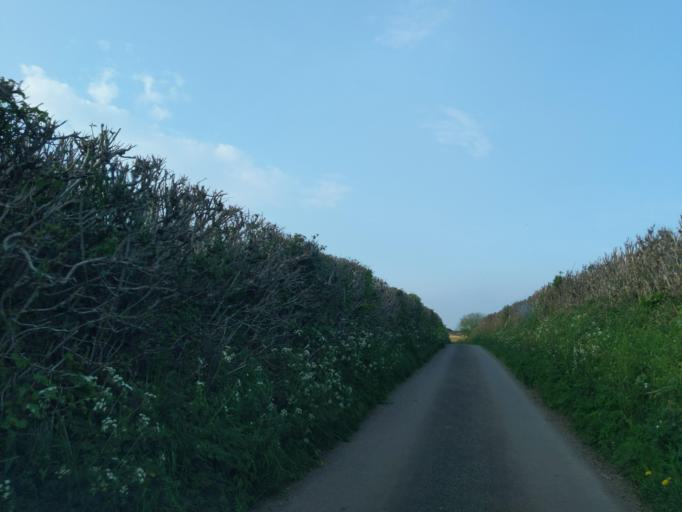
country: GB
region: England
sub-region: Devon
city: Yealmpton
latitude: 50.3531
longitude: -4.0399
